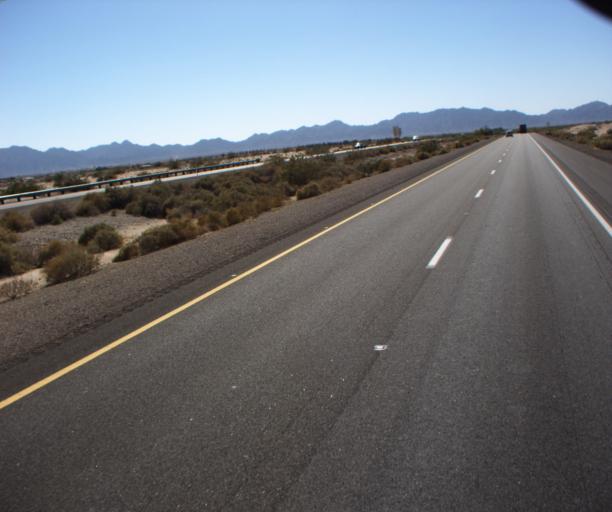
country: US
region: Arizona
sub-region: Yuma County
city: Wellton
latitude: 32.6599
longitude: -114.1513
